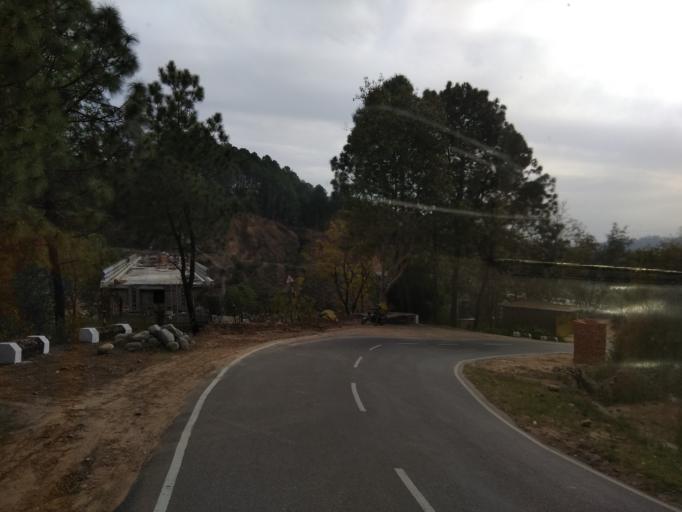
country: IN
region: Himachal Pradesh
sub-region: Kangra
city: Palampur
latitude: 32.1113
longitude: 76.4882
